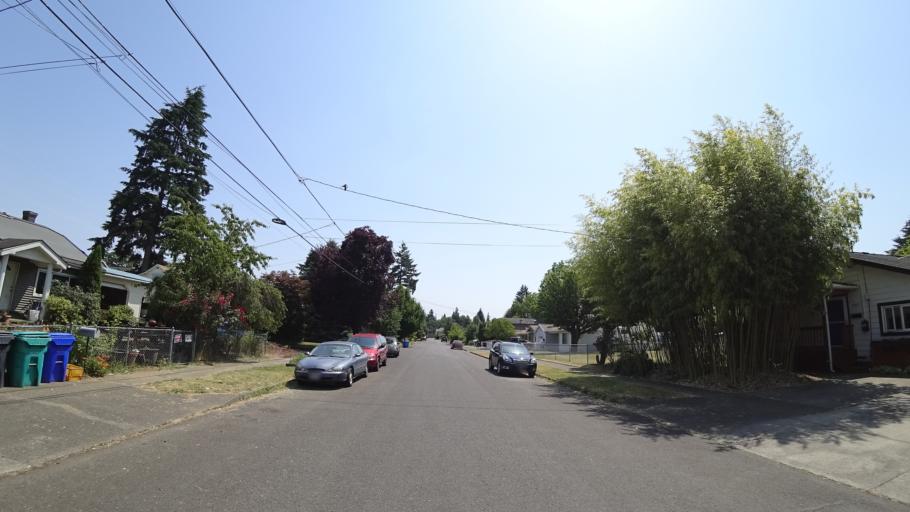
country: US
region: Washington
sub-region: Clark County
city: Vancouver
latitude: 45.5866
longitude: -122.6962
